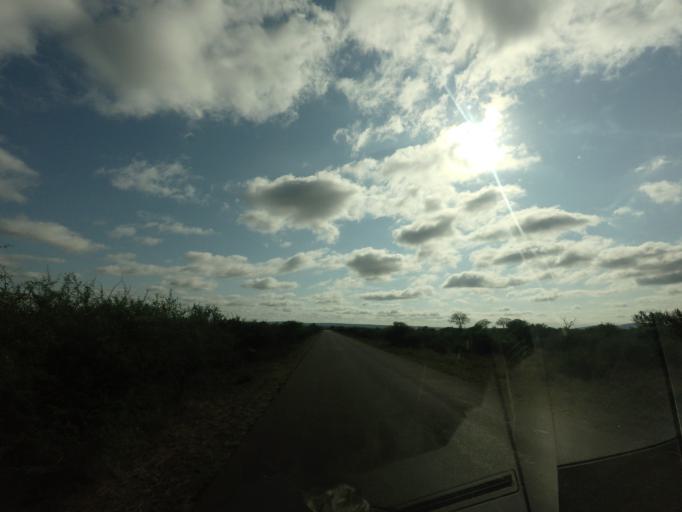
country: ZA
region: Mpumalanga
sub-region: Ehlanzeni District
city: Komatipoort
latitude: -25.1666
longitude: 31.9239
